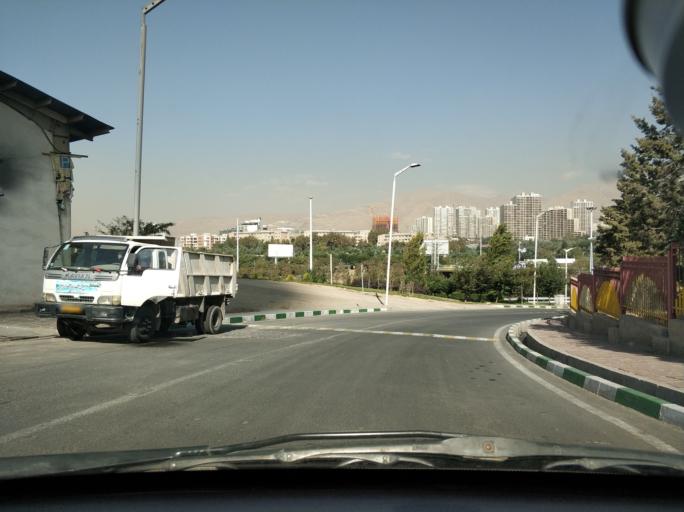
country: IR
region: Tehran
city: Tehran
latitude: 35.7472
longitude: 51.3728
